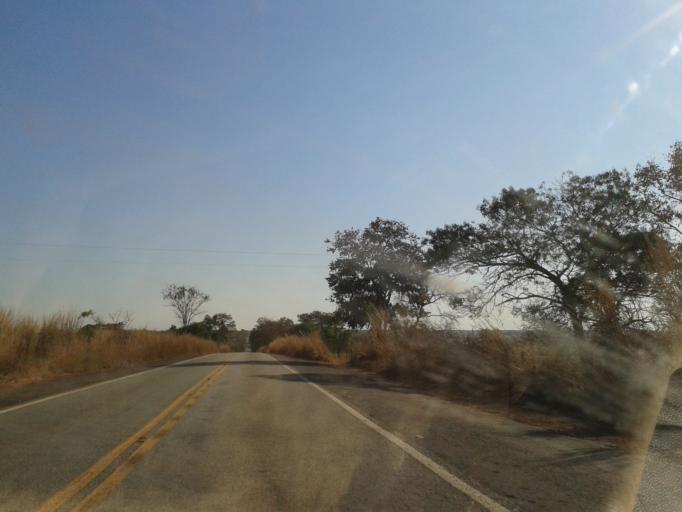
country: BR
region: Goias
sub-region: Mozarlandia
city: Mozarlandia
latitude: -14.9689
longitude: -50.5801
